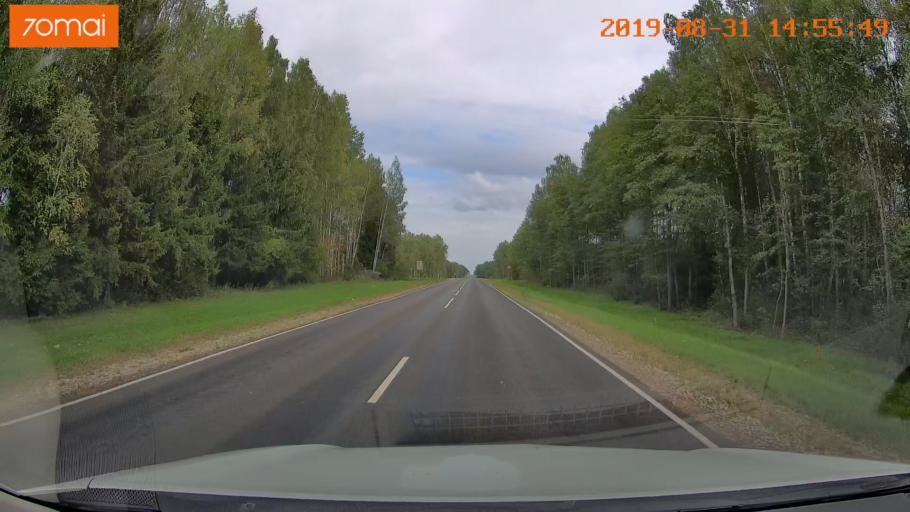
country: RU
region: Kaluga
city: Spas-Demensk
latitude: 54.3006
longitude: 33.9235
